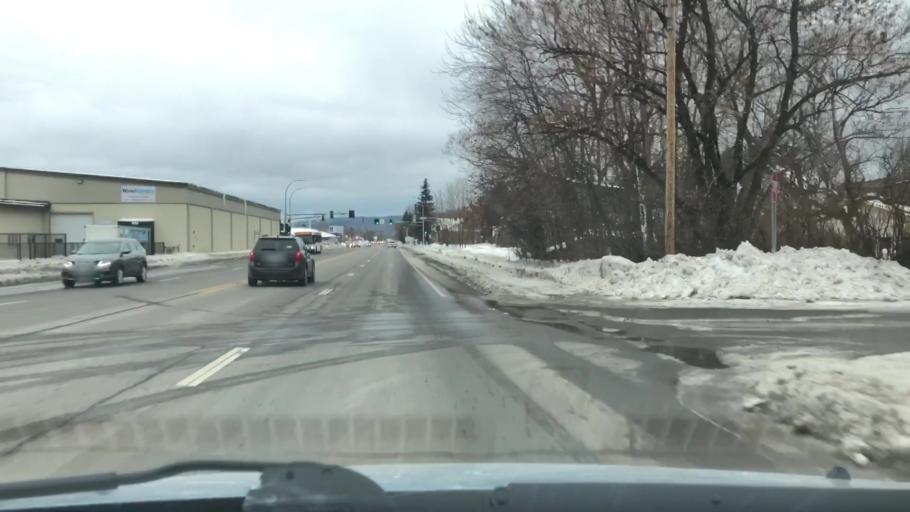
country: US
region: Minnesota
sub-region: Saint Louis County
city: Proctor
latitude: 46.7324
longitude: -92.1785
